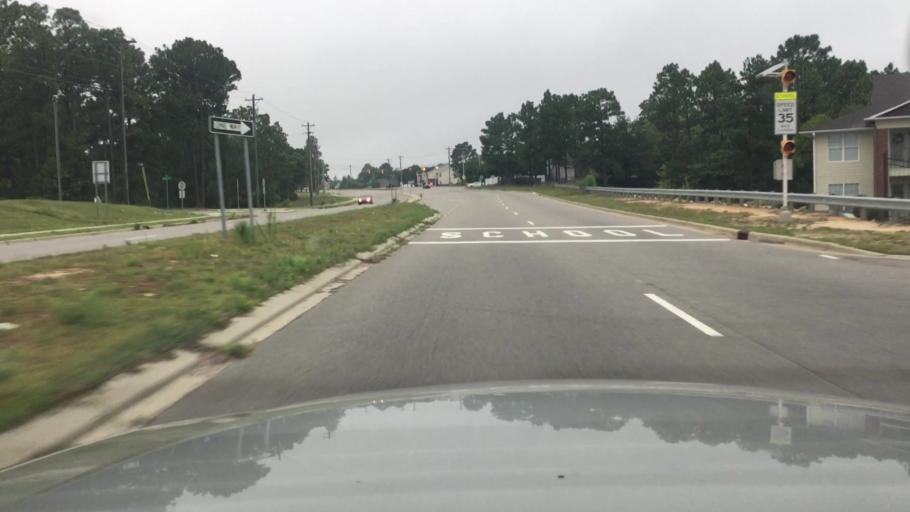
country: US
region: North Carolina
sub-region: Cumberland County
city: Hope Mills
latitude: 34.9762
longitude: -78.9226
